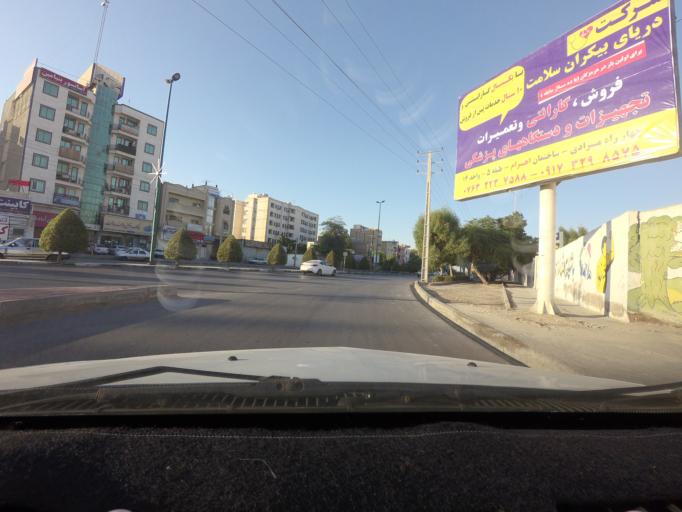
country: IR
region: Hormozgan
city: Bandar 'Abbas
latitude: 27.1755
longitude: 56.2598
